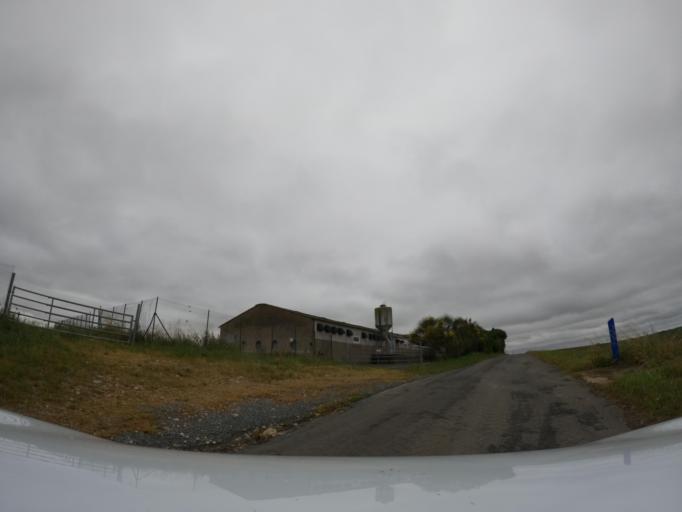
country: FR
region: Pays de la Loire
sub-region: Departement de la Vendee
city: Saint-Hilaire-des-Loges
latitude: 46.4285
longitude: -0.7041
